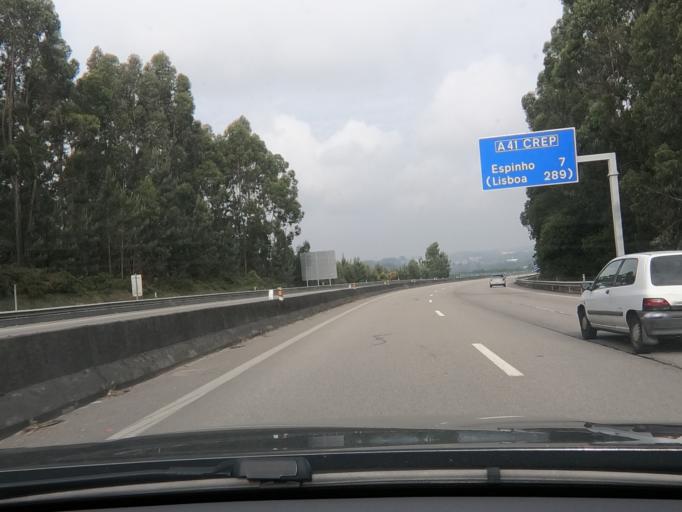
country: PT
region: Porto
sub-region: Vila Nova de Gaia
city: Grijo
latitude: 41.0101
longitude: -8.5646
